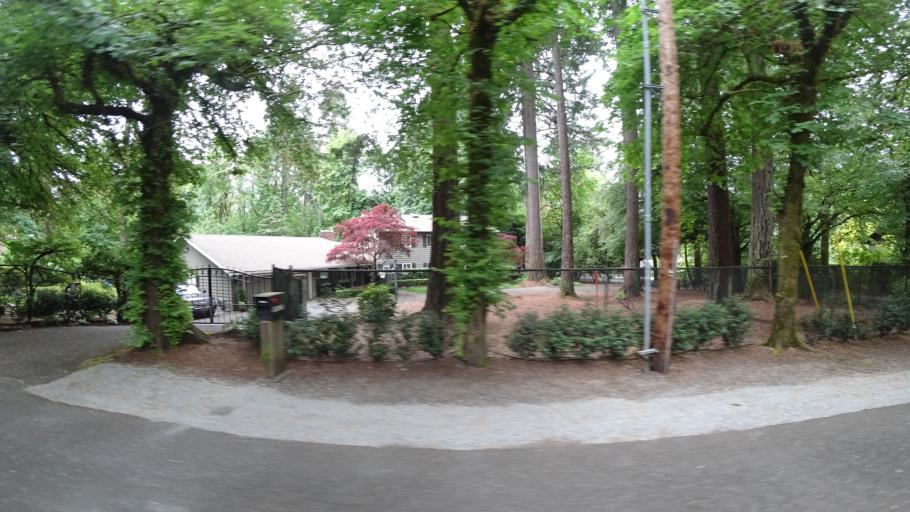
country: US
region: Oregon
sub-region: Clackamas County
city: Lake Oswego
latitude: 45.4320
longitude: -122.6635
